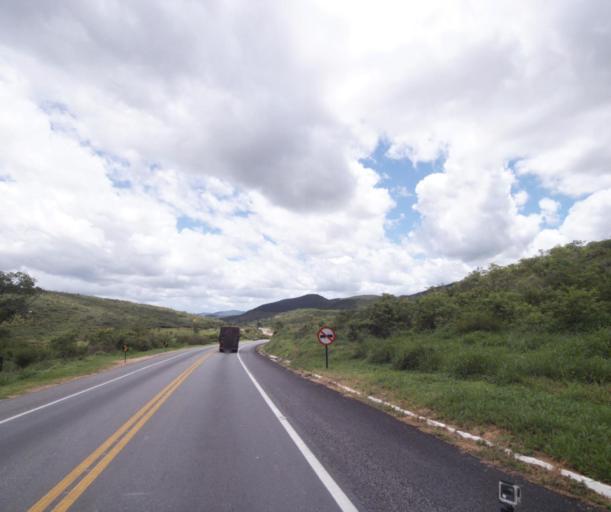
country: BR
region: Bahia
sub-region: Pocoes
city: Pocoes
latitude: -14.3638
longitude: -40.3428
